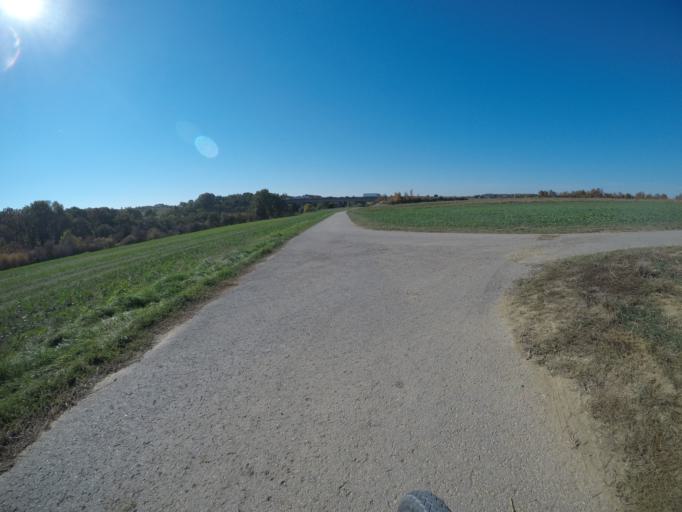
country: DE
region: Baden-Wuerttemberg
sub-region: Regierungsbezirk Stuttgart
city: Bondorf
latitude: 48.5398
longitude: 8.8945
